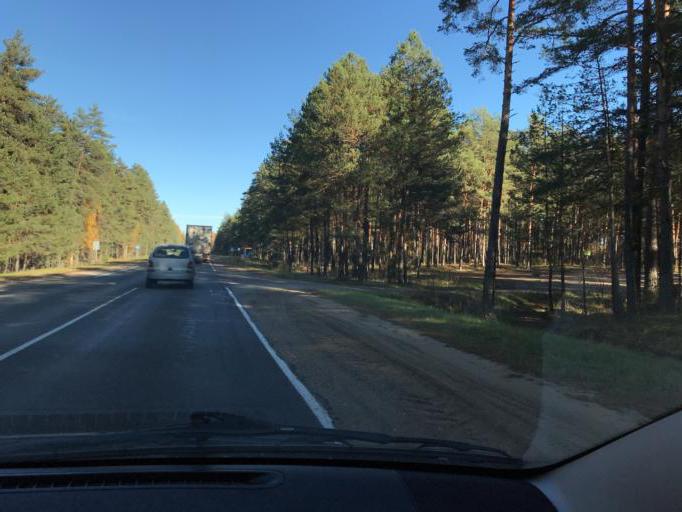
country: BY
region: Vitebsk
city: Polatsk
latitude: 55.3457
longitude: 28.7970
